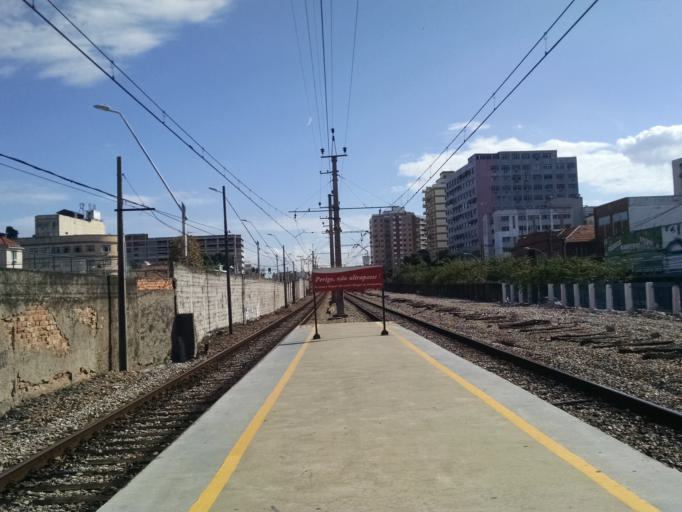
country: BR
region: Rio de Janeiro
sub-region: Duque De Caxias
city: Duque de Caxias
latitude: -22.8466
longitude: -43.2668
